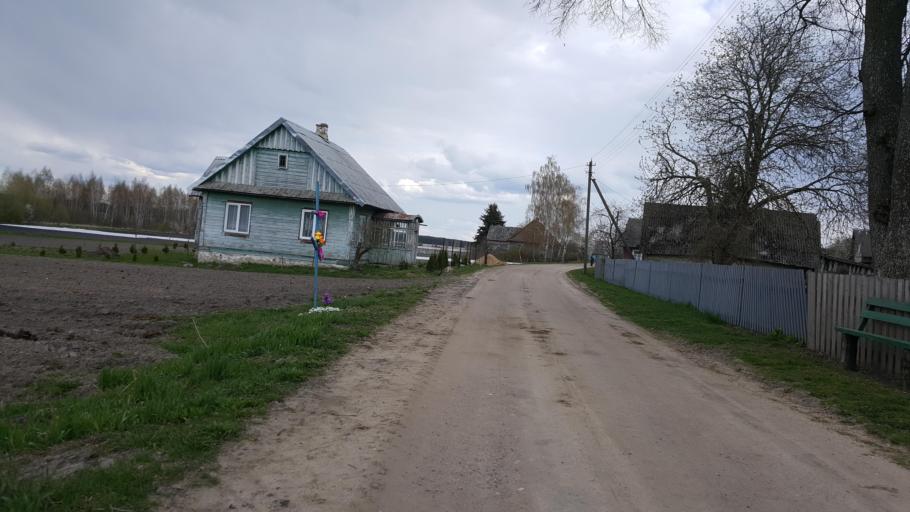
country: BY
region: Brest
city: Kamyanyets
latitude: 52.4063
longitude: 23.7163
